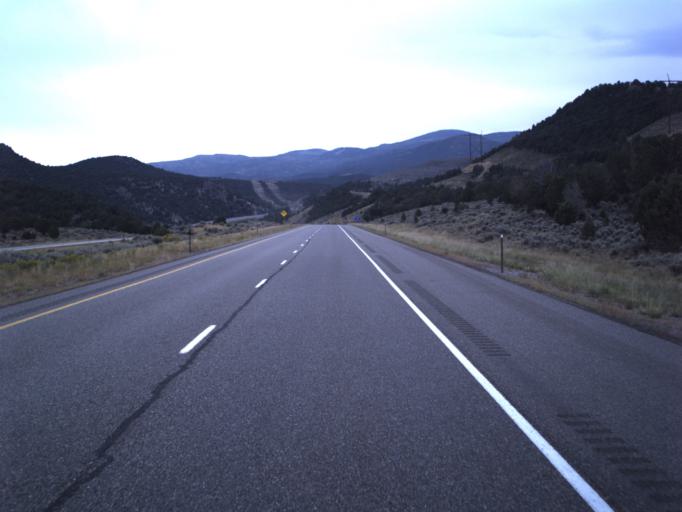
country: US
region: Utah
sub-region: Sevier County
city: Monroe
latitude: 38.5677
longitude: -112.4453
